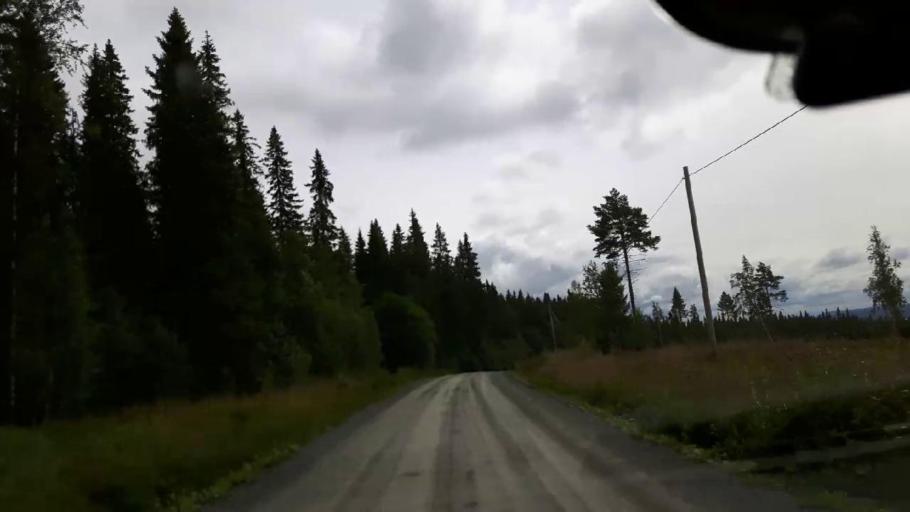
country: SE
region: Jaemtland
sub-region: Krokoms Kommun
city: Valla
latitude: 63.6788
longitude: 13.9302
